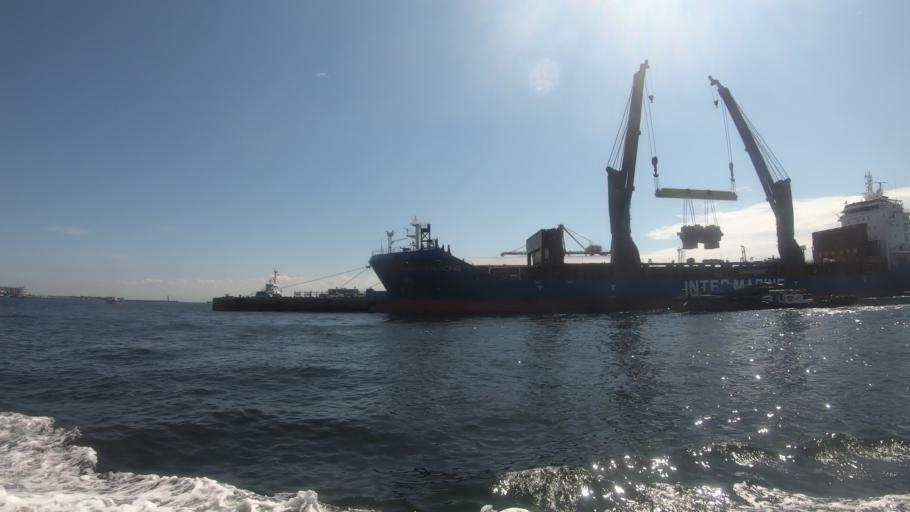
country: JP
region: Kanagawa
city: Yokohama
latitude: 35.4456
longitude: 139.6739
